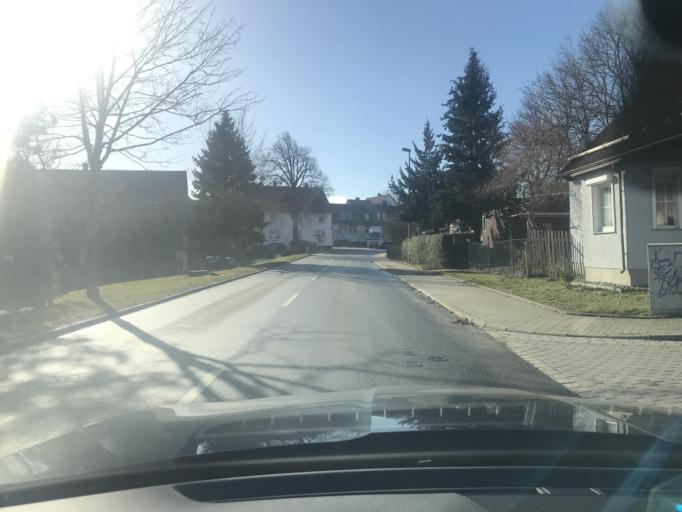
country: DE
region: Saxony-Anhalt
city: Huttenrode
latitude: 51.7721
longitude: 10.9065
